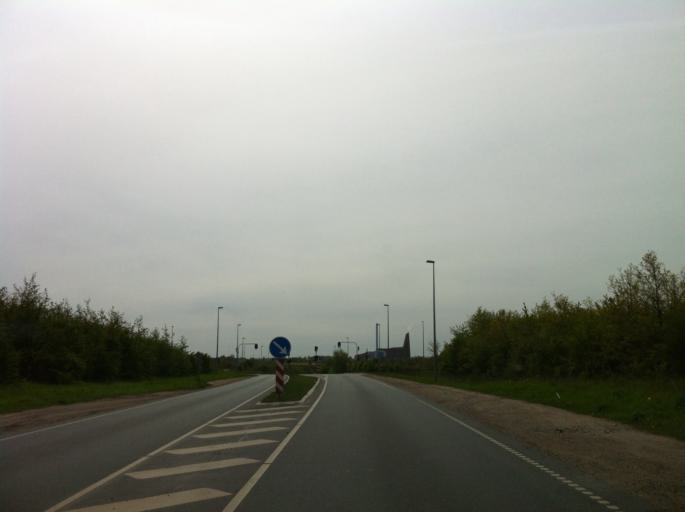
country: DK
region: Zealand
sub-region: Roskilde Kommune
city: Roskilde
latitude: 55.6640
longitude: 12.1170
